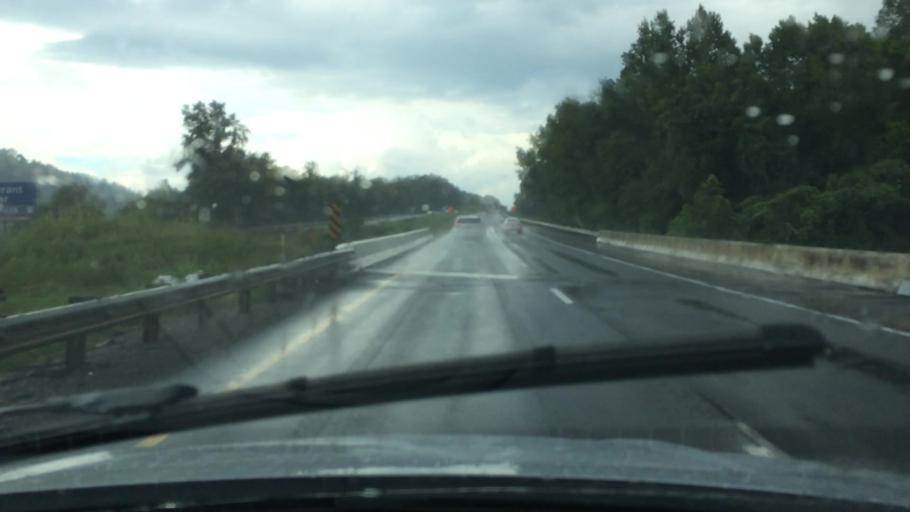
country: US
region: Tennessee
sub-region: Cocke County
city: Newport
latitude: 35.8435
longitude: -83.1819
